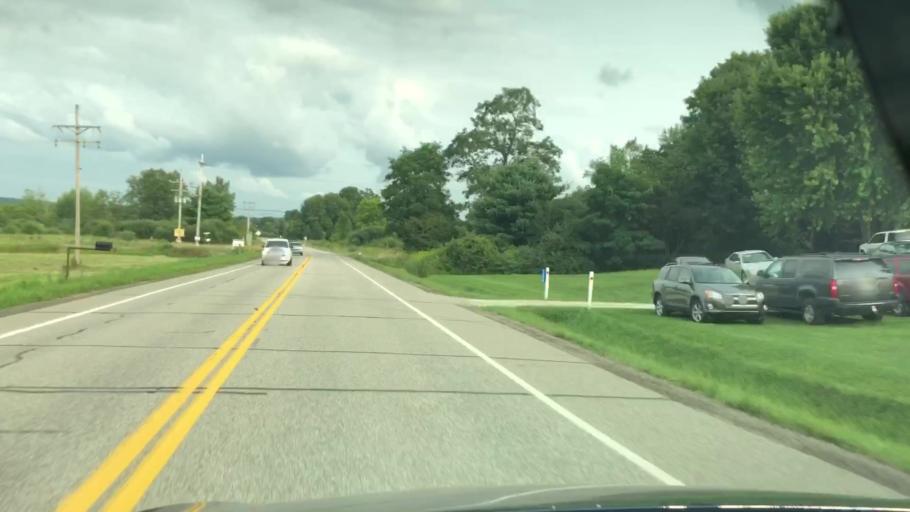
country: US
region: Pennsylvania
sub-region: Erie County
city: Northwest Harborcreek
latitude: 42.0589
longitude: -79.8648
